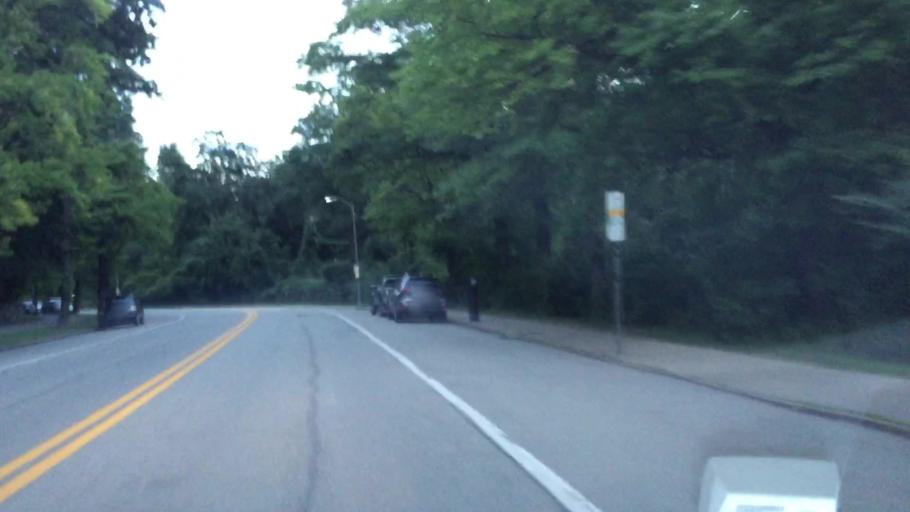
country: US
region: Pennsylvania
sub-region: Allegheny County
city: Bloomfield
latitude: 40.4387
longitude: -79.9451
